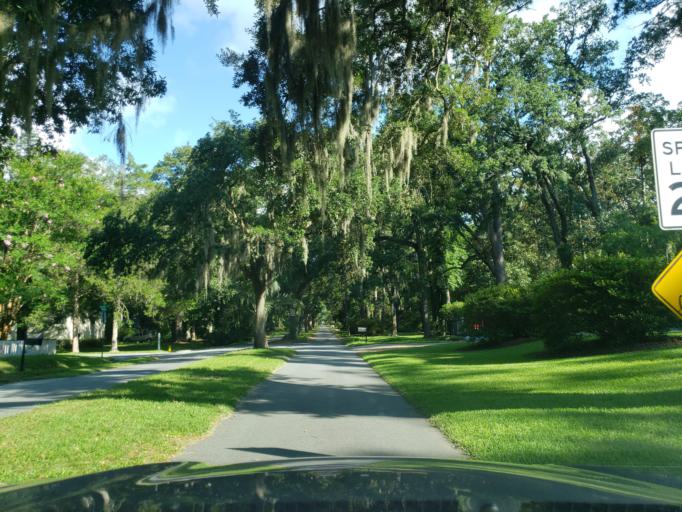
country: US
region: Georgia
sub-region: Chatham County
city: Isle of Hope
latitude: 31.9742
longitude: -81.0581
